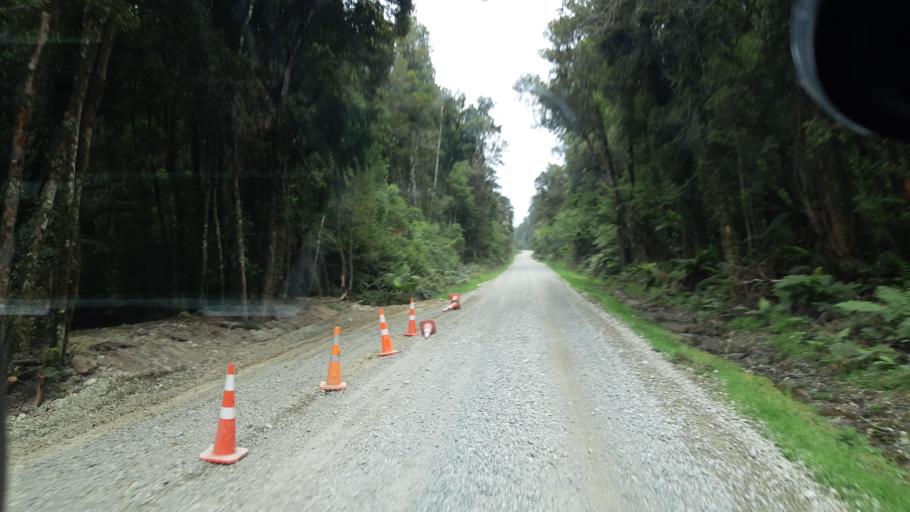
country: NZ
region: West Coast
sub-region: Grey District
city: Greymouth
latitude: -42.6469
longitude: 171.3342
